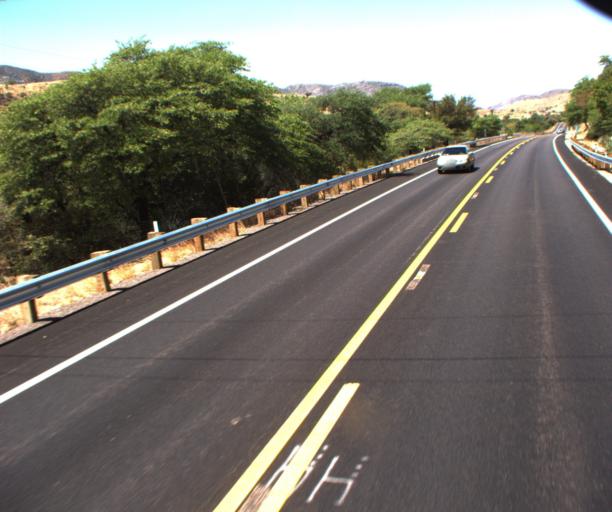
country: US
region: Arizona
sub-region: Cochise County
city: Bisbee
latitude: 31.4841
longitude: -109.9837
